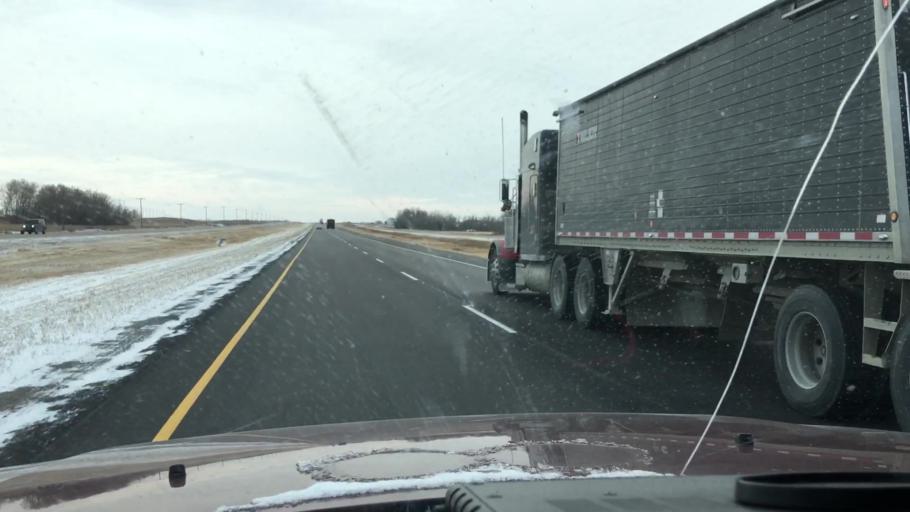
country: CA
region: Saskatchewan
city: Saskatoon
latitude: 51.9392
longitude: -106.5396
